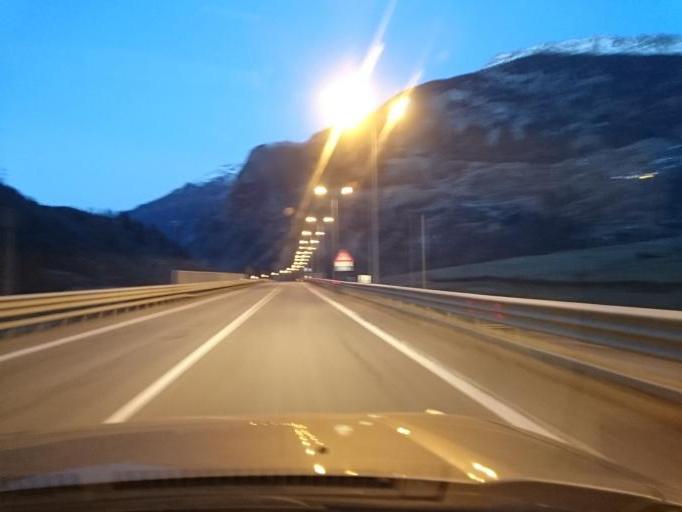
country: IT
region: Lombardy
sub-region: Provincia di Sondrio
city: Sondalo
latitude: 46.3456
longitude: 10.3516
